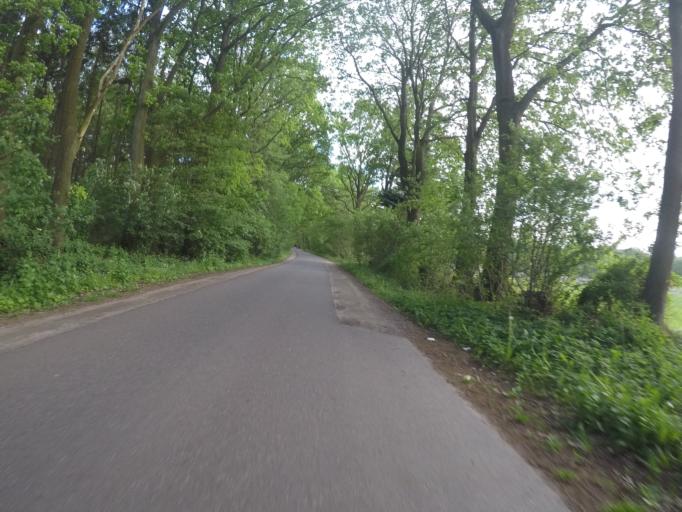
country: DE
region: Schleswig-Holstein
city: Bonningstedt
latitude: 53.6572
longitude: 9.9267
